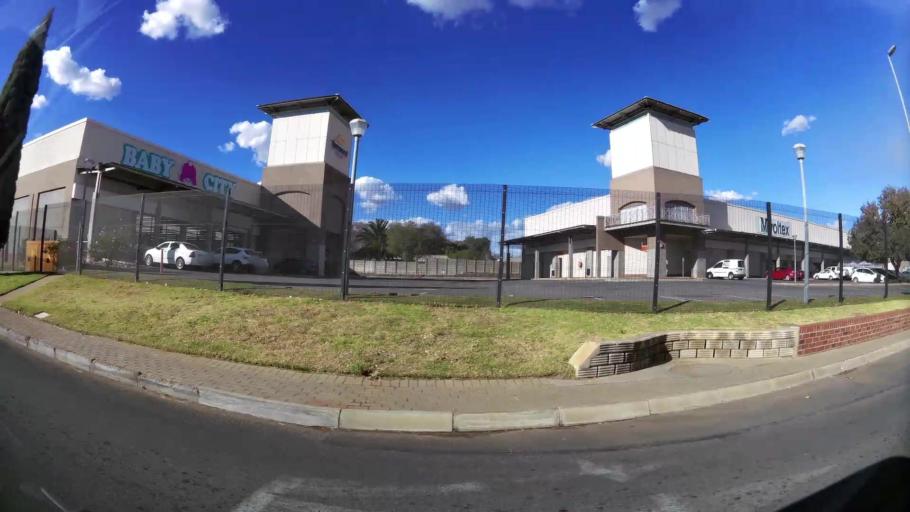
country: ZA
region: North-West
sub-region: Dr Kenneth Kaunda District Municipality
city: Klerksdorp
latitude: -26.8541
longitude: 26.6772
